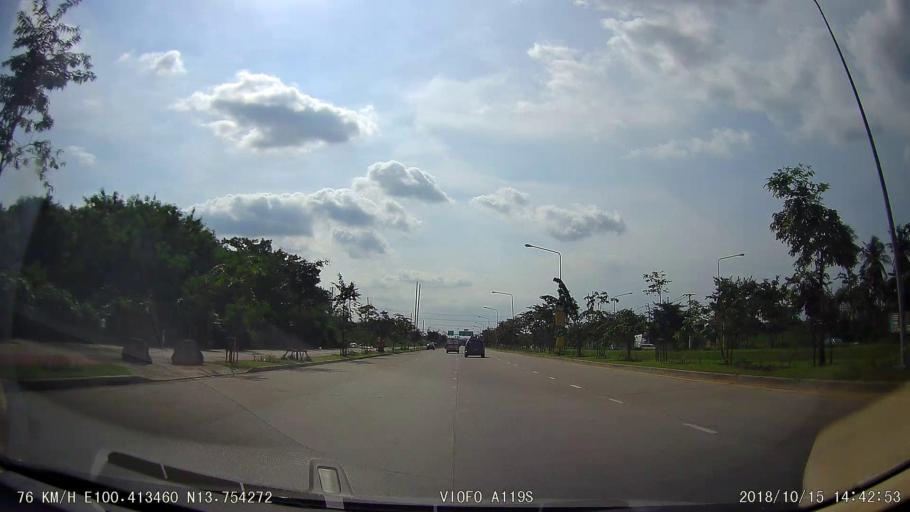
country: TH
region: Bangkok
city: Phasi Charoen
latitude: 13.7543
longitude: 100.4132
